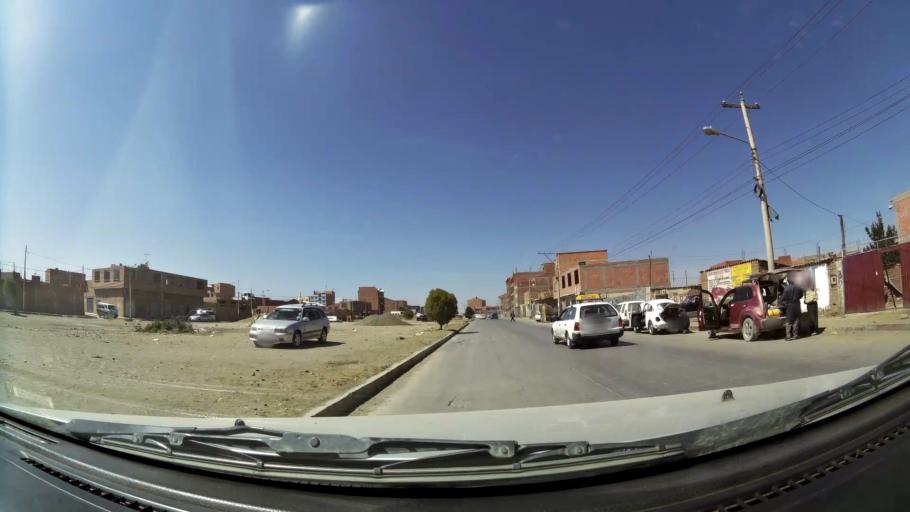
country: BO
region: La Paz
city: La Paz
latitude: -16.5495
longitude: -68.1909
